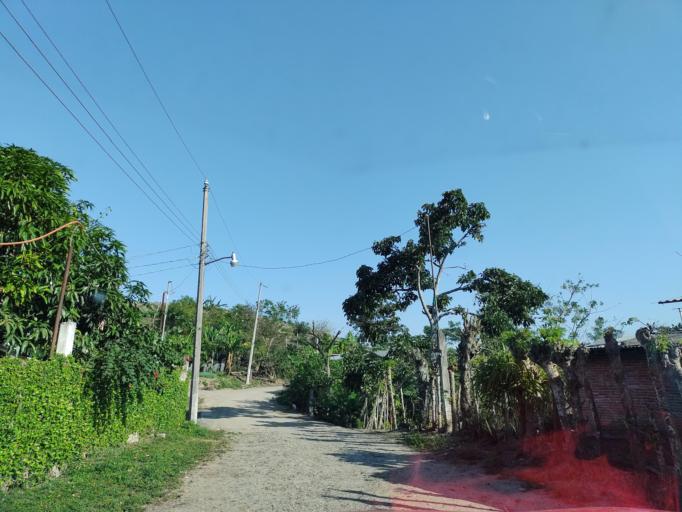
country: MX
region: Veracruz
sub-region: Papantla
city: Polutla
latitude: 20.4560
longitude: -97.2263
